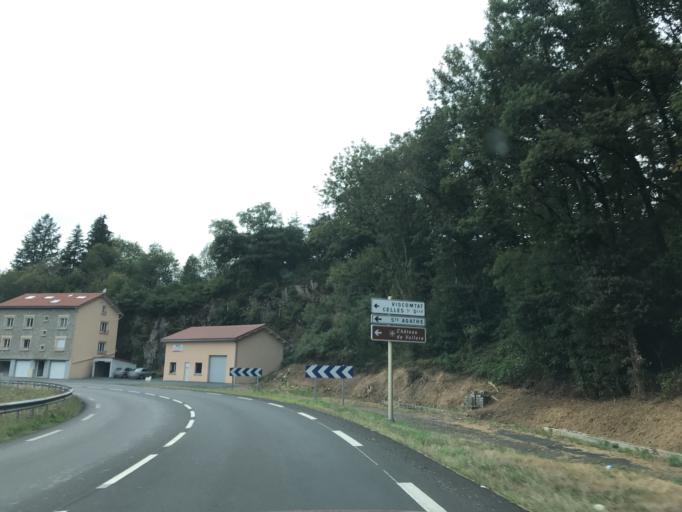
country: FR
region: Auvergne
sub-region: Departement du Puy-de-Dome
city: Celles-sur-Durolle
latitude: 45.8676
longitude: 3.6388
